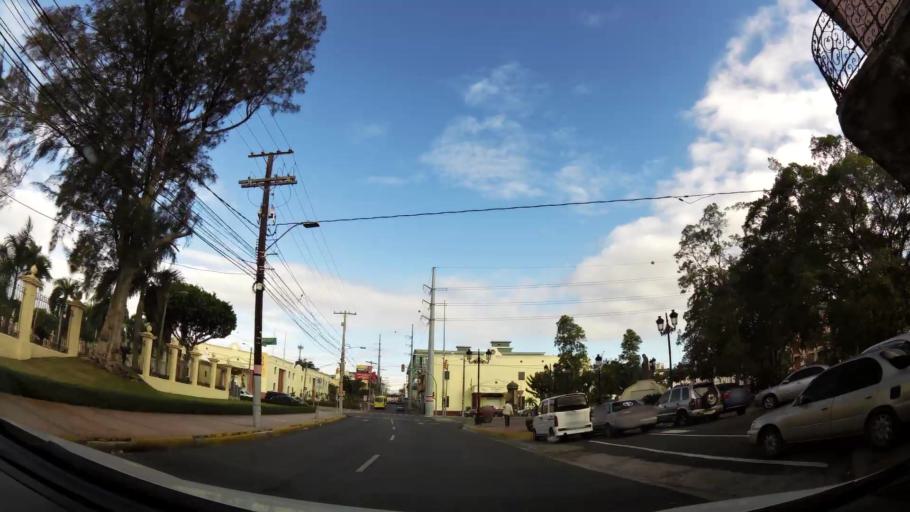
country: DO
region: Nacional
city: San Carlos
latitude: 18.4759
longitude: -69.8963
